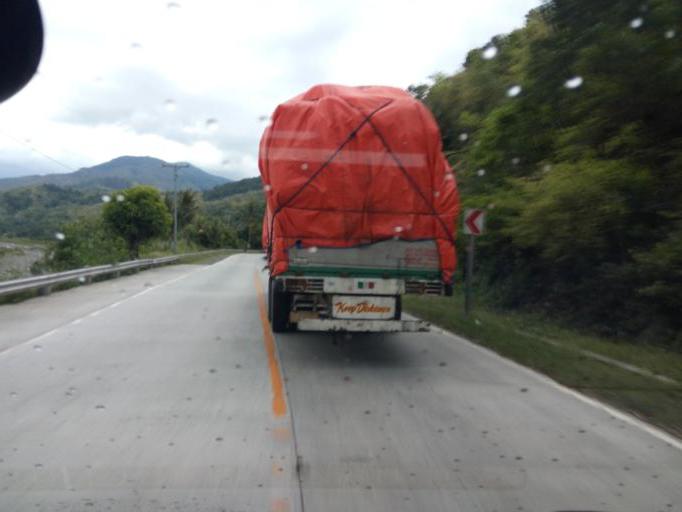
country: PH
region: Central Luzon
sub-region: Province of Nueva Ecija
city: Burgos
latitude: 16.0583
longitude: 120.9496
